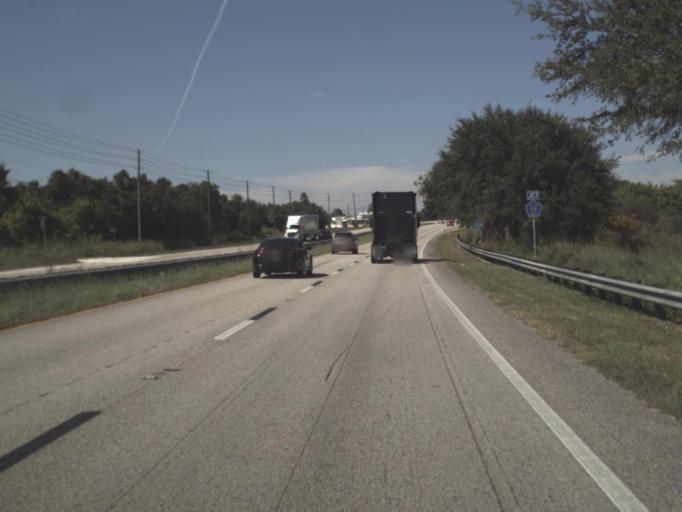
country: US
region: Florida
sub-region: Highlands County
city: Lake Placid
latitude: 27.2831
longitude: -81.3563
